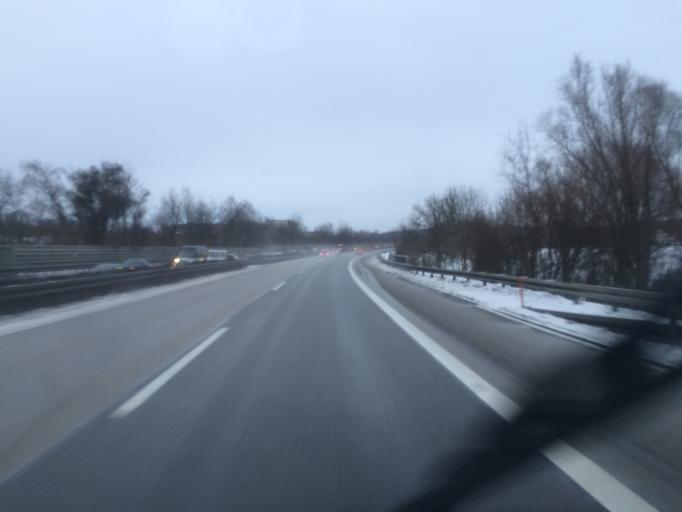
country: DE
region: Bavaria
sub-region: Upper Palatinate
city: Lappersdorf
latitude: 49.0503
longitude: 12.0924
